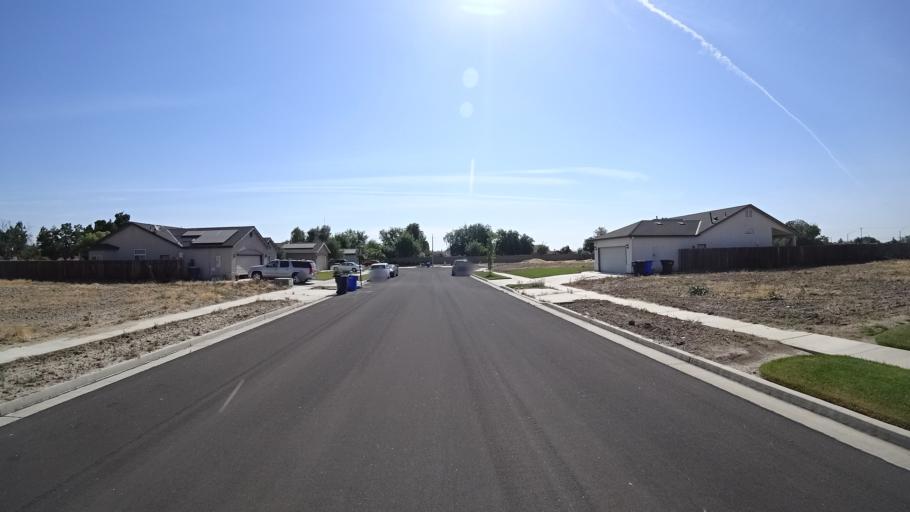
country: US
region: California
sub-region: Kings County
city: Hanford
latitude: 36.3446
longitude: -119.6674
